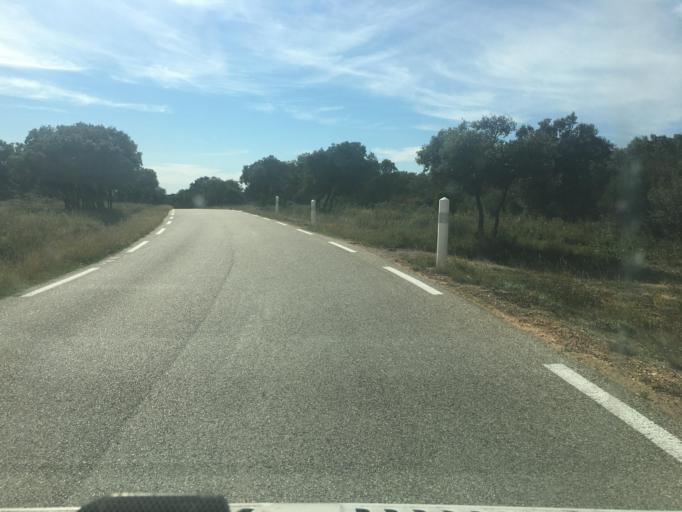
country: FR
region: Languedoc-Roussillon
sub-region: Departement du Gard
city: Saint-Quentin-la-Poterie
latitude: 44.0316
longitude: 4.5107
